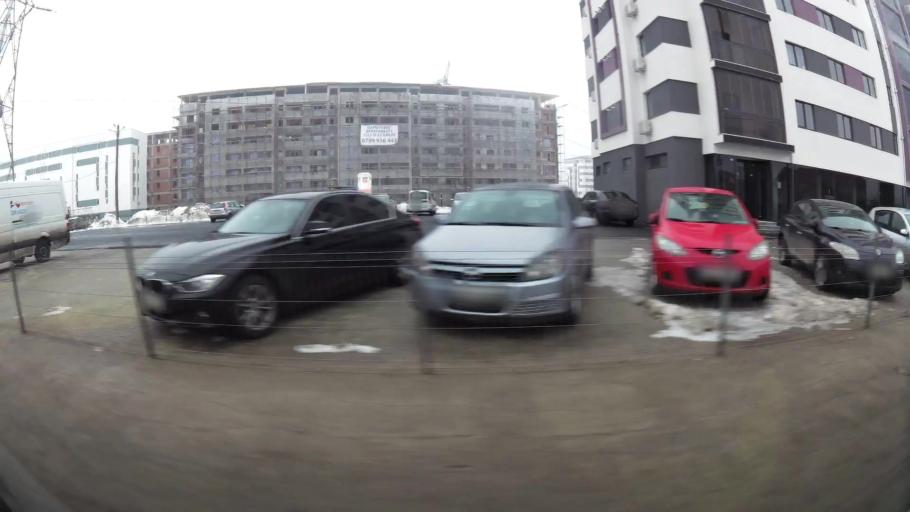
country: RO
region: Ilfov
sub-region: Comuna Chiajna
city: Rosu
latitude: 44.4483
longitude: 25.9910
